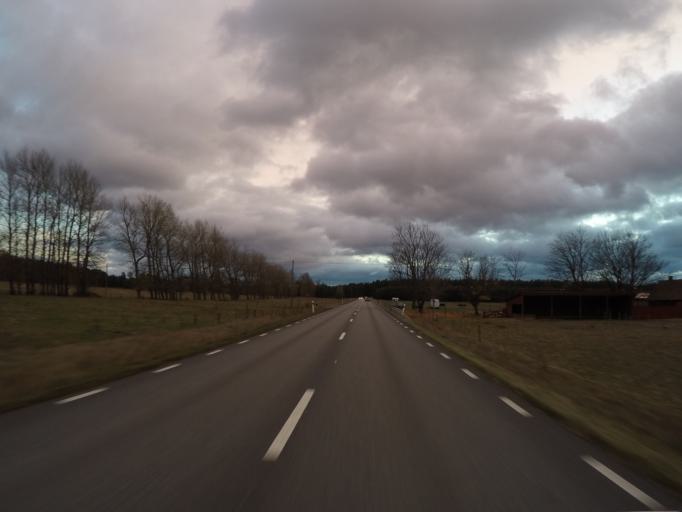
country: SE
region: Skane
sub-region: Kristianstads Kommun
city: Degeberga
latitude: 55.8829
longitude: 14.0871
